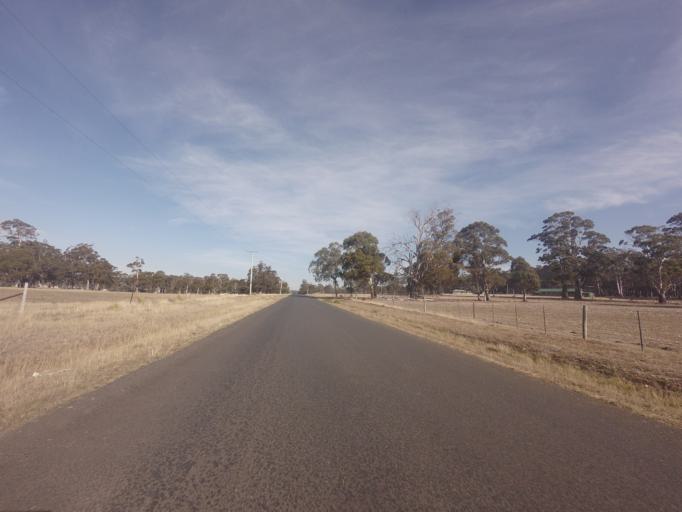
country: AU
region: Tasmania
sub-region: Sorell
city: Sorell
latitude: -42.4609
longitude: 147.4614
